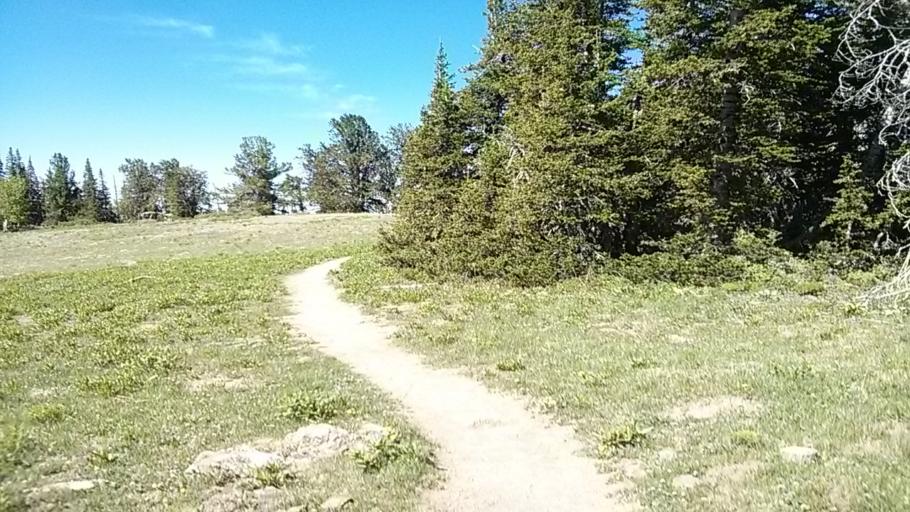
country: US
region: Utah
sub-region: Iron County
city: Parowan
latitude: 37.6332
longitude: -112.8312
